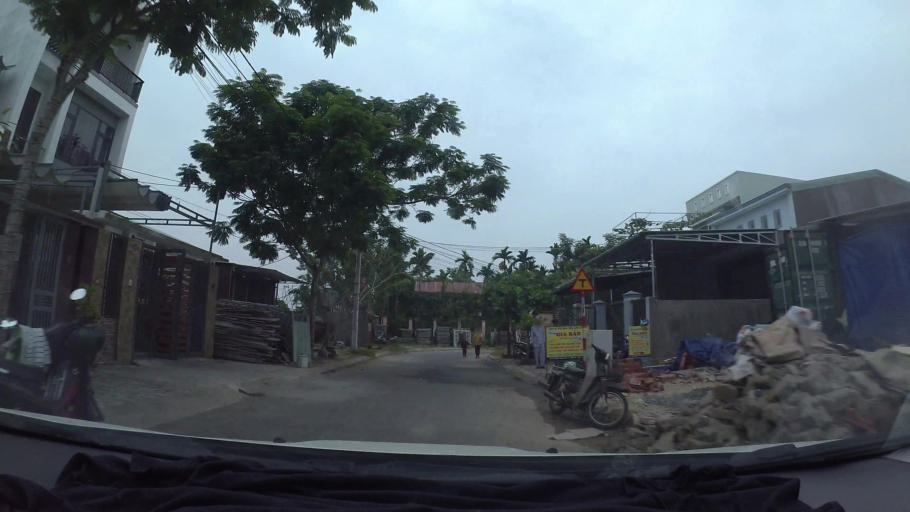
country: VN
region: Da Nang
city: Thanh Khe
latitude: 16.0470
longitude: 108.1759
